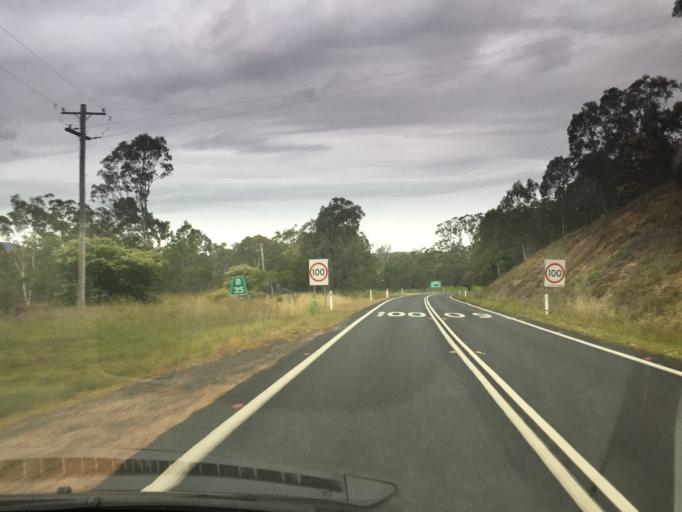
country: AU
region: New South Wales
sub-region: Bega Valley
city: Bega
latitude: -36.6318
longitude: 149.5755
